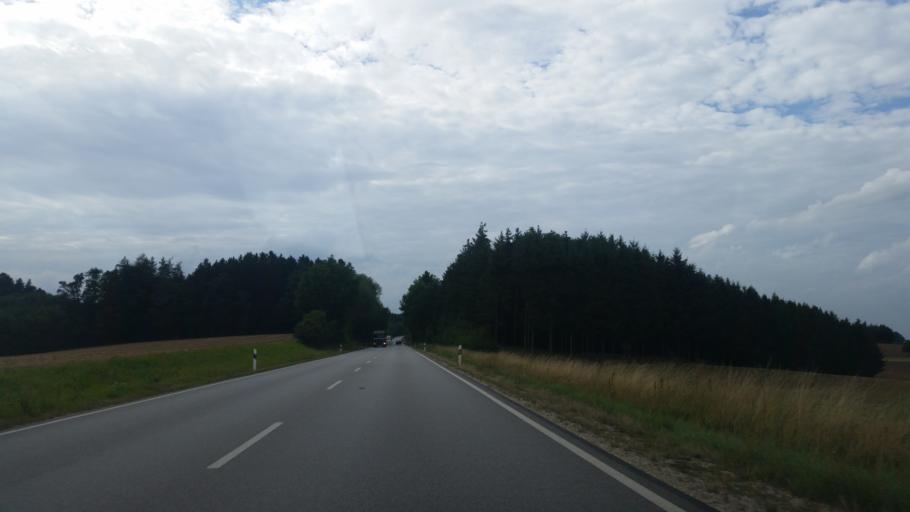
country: DE
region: Bavaria
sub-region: Lower Bavaria
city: Geisenhausen
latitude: 48.4981
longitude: 12.2218
